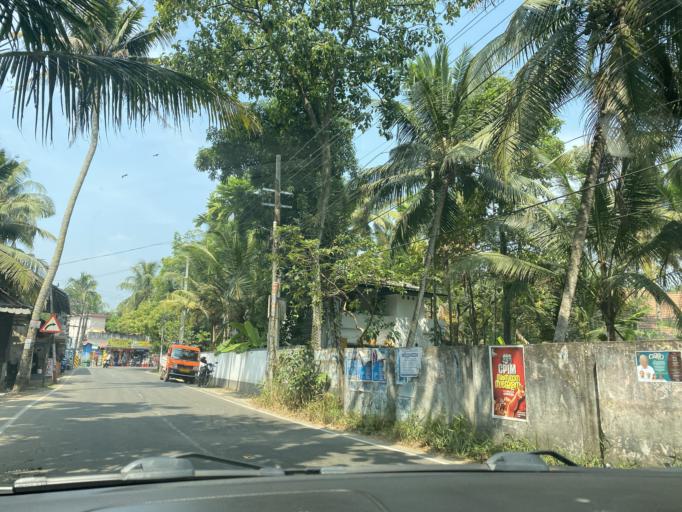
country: IN
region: Kerala
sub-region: Alappuzha
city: Arukutti
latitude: 9.9054
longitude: 76.3208
